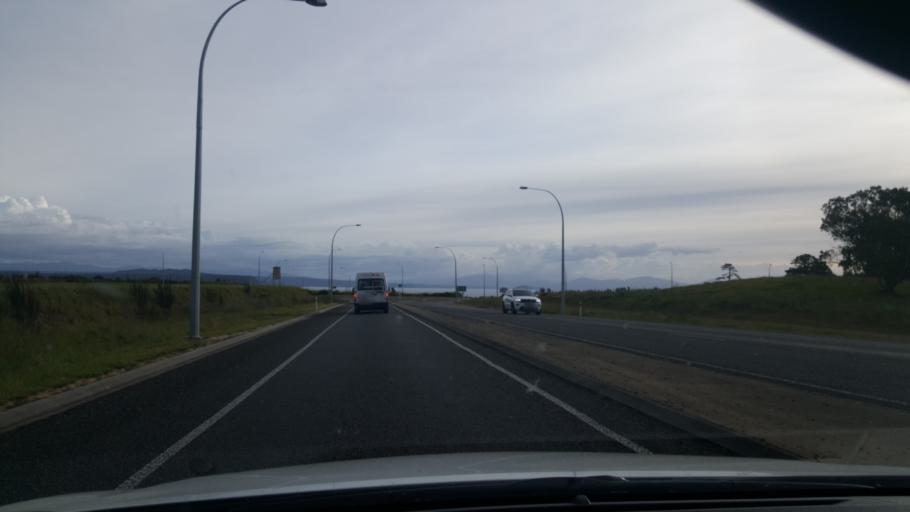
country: NZ
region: Waikato
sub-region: Taupo District
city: Taupo
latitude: -38.7374
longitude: 176.0739
